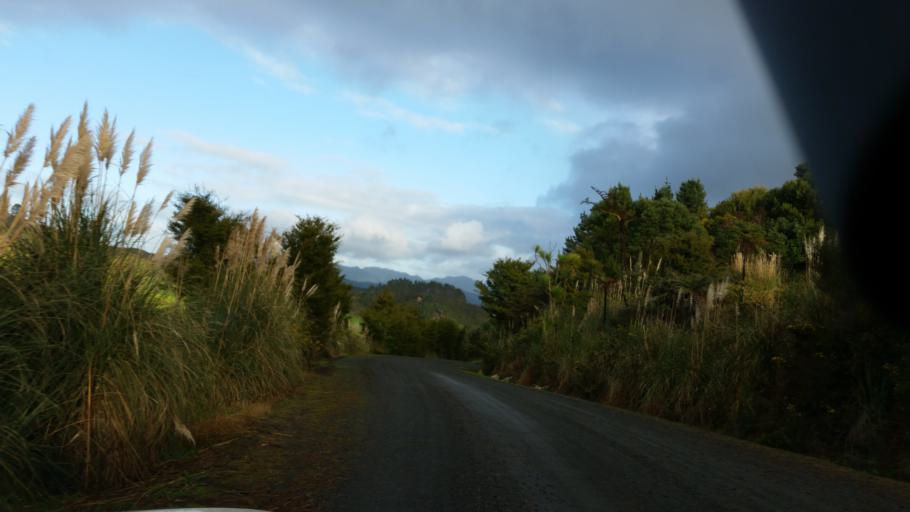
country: NZ
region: Northland
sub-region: Whangarei
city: Maungatapere
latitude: -35.7563
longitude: 174.0924
